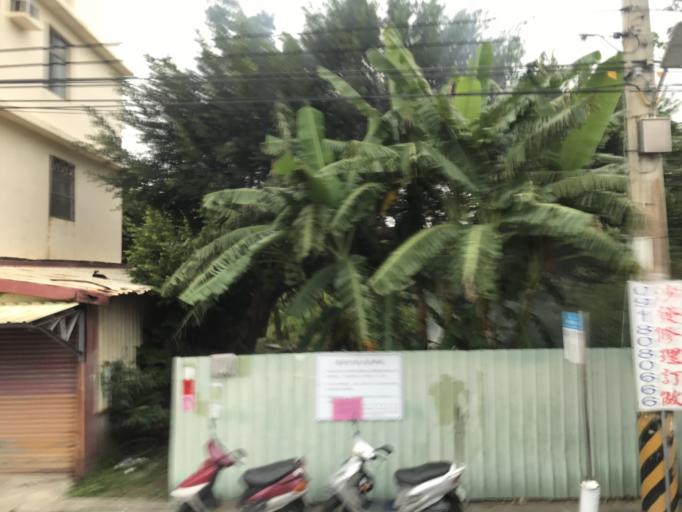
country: TW
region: Taiwan
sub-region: Hsinchu
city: Hsinchu
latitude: 24.8391
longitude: 120.9395
